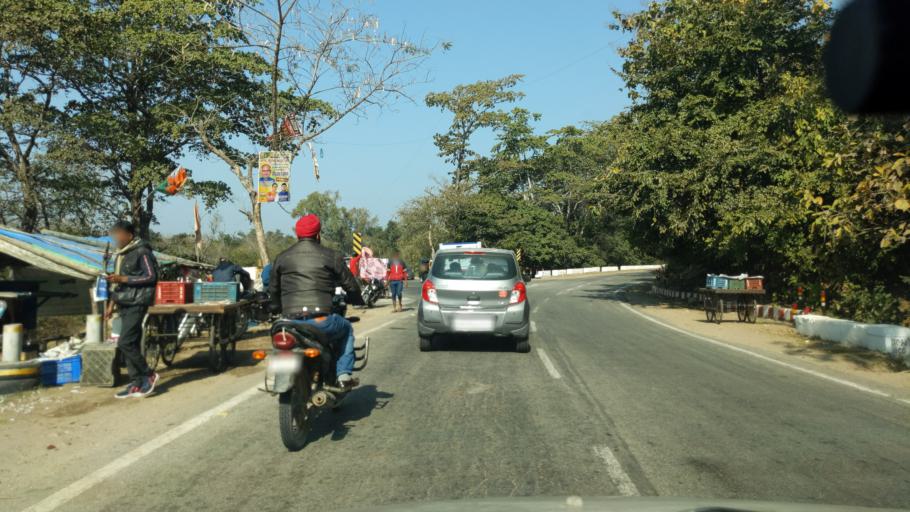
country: IN
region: Uttarakhand
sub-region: Naini Tal
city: Ramnagar
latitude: 29.3905
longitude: 79.1381
